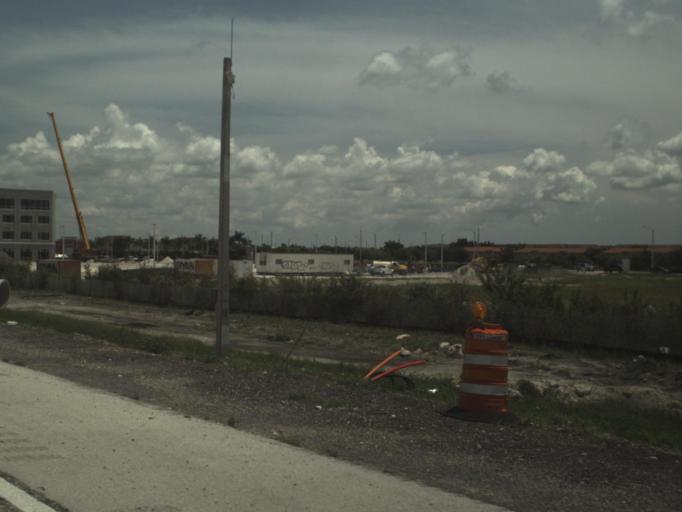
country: US
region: Florida
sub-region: Broward County
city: Sunshine Ranches
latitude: 25.9987
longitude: -80.3390
